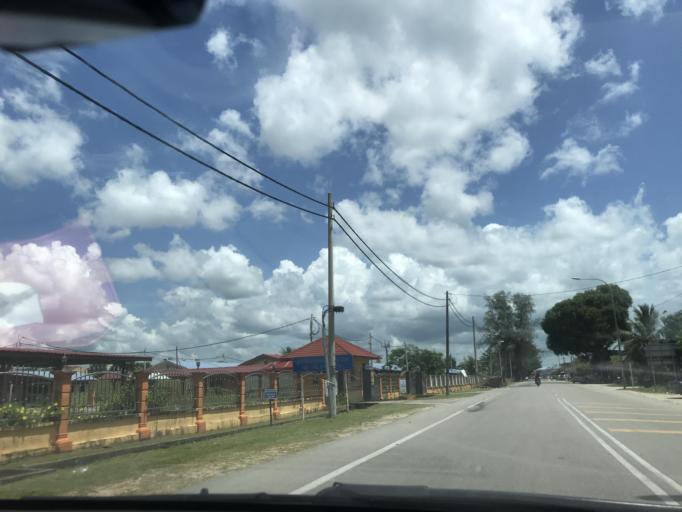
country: TH
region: Narathiwat
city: Tak Bai
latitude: 6.2307
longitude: 102.0948
